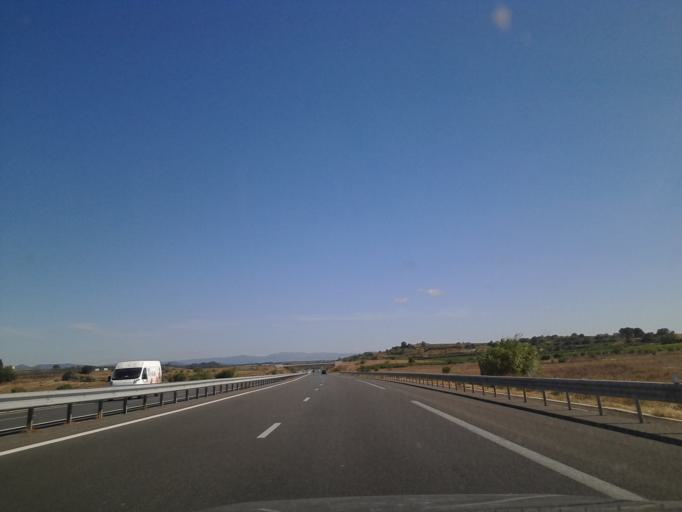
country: FR
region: Languedoc-Roussillon
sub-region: Departement de l'Herault
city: Valros
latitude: 43.4231
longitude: 3.3884
